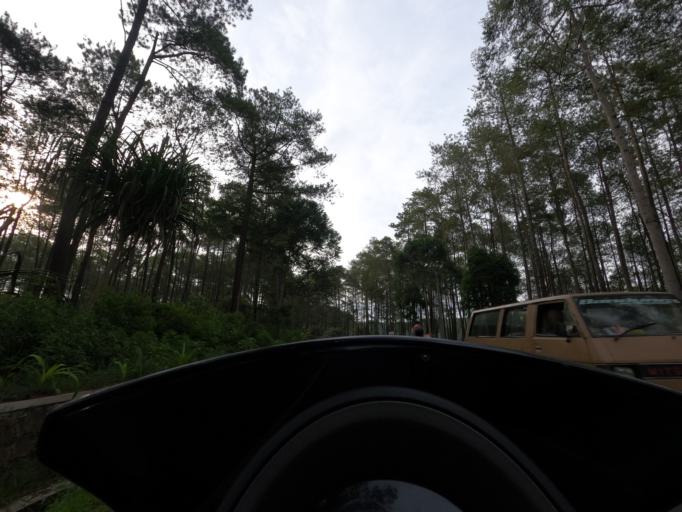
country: ID
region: West Java
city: Lembang
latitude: -6.7806
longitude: 107.6459
